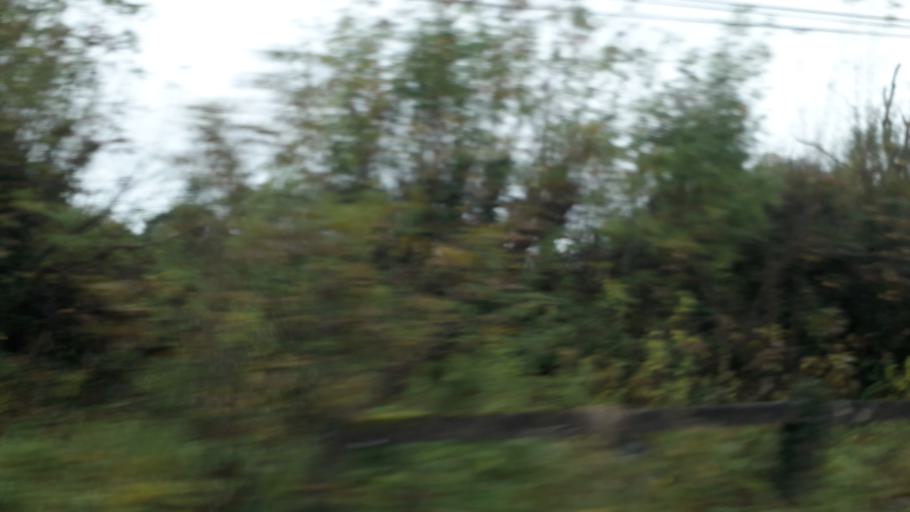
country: IE
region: Connaught
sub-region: Roscommon
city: Ballaghaderreen
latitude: 53.8909
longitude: -8.5496
